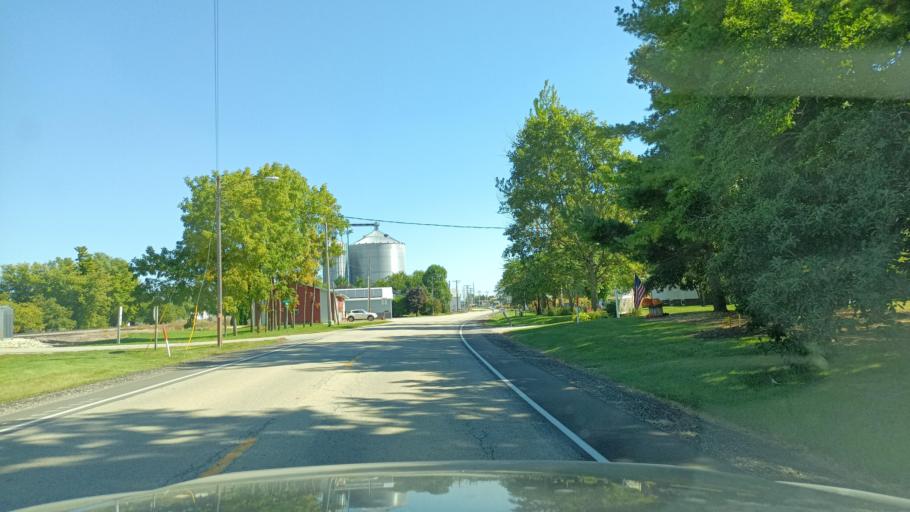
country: US
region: Illinois
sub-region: Woodford County
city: Eureka
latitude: 40.6282
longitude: -89.2826
